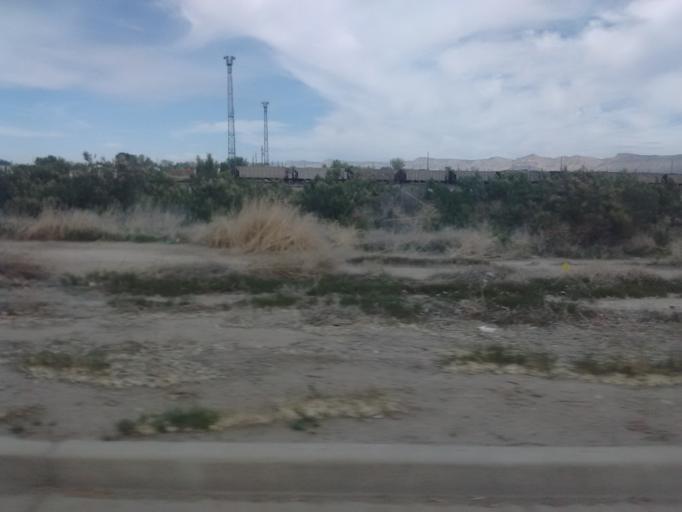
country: US
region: Colorado
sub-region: Mesa County
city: Grand Junction
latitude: 39.0630
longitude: -108.5423
